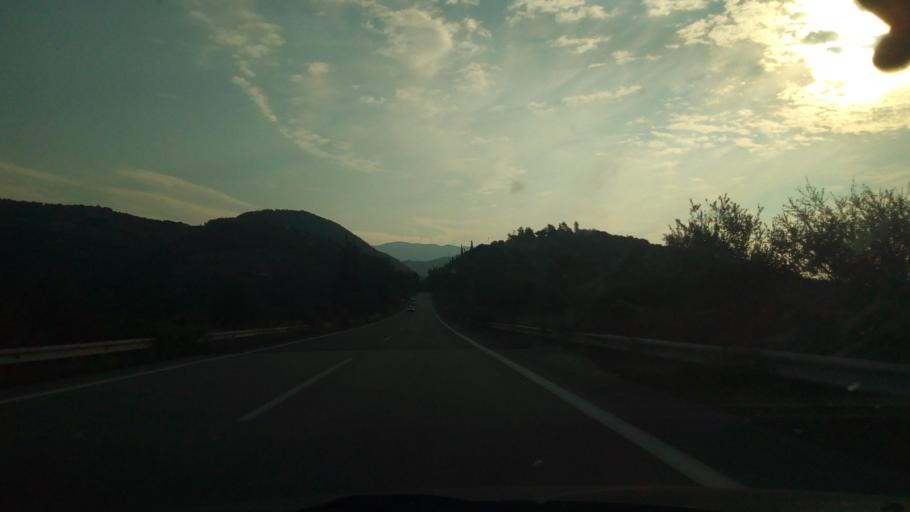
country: GR
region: West Greece
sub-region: Nomos Aitolias kai Akarnanias
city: Nafpaktos
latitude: 38.4042
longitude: 21.9204
